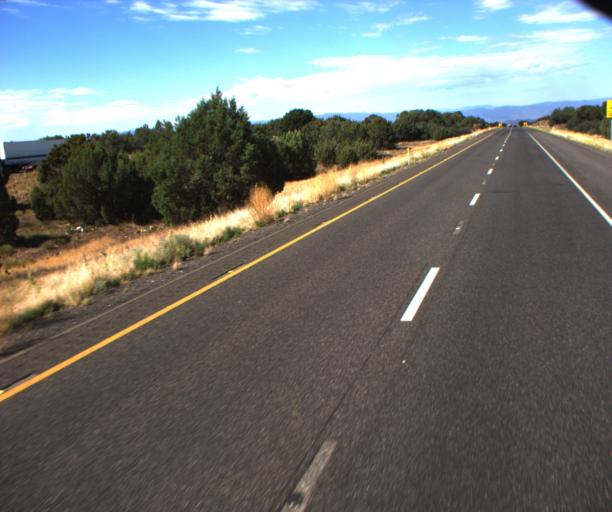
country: US
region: Arizona
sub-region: Yavapai County
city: Village of Oak Creek (Big Park)
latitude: 34.7555
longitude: -111.6695
